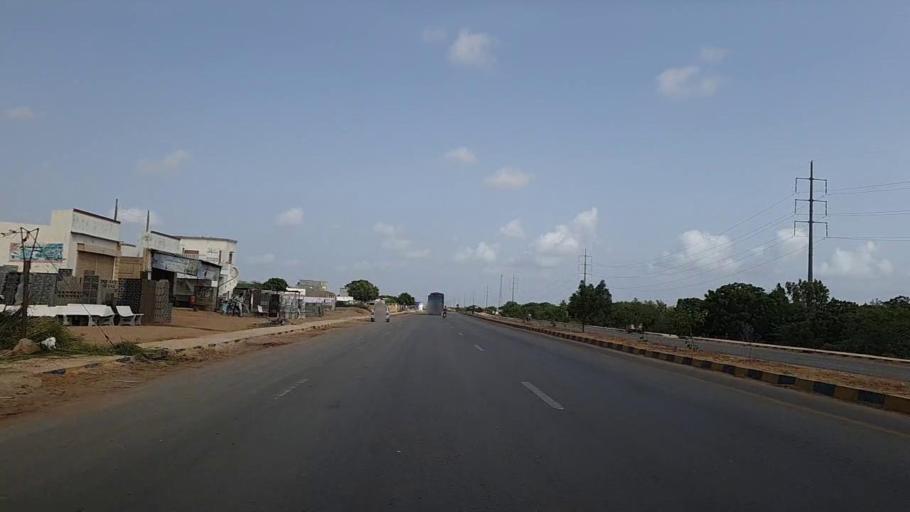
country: PK
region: Sindh
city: Gharo
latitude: 24.7861
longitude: 67.5309
